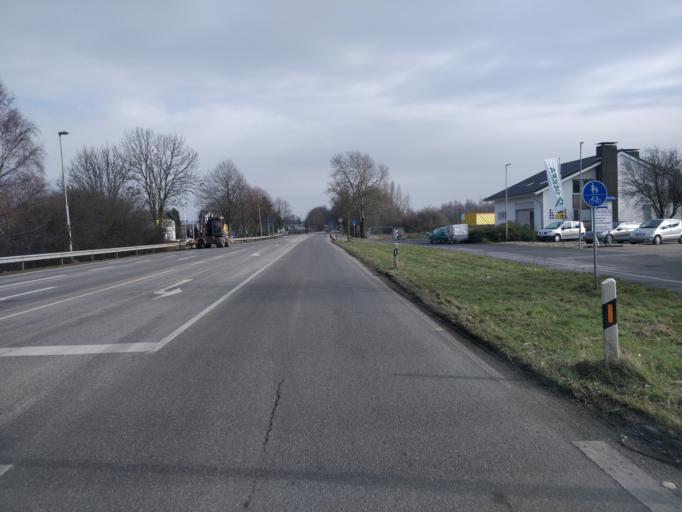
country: DE
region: North Rhine-Westphalia
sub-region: Regierungsbezirk Dusseldorf
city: Emmerich
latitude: 51.8310
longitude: 6.2746
